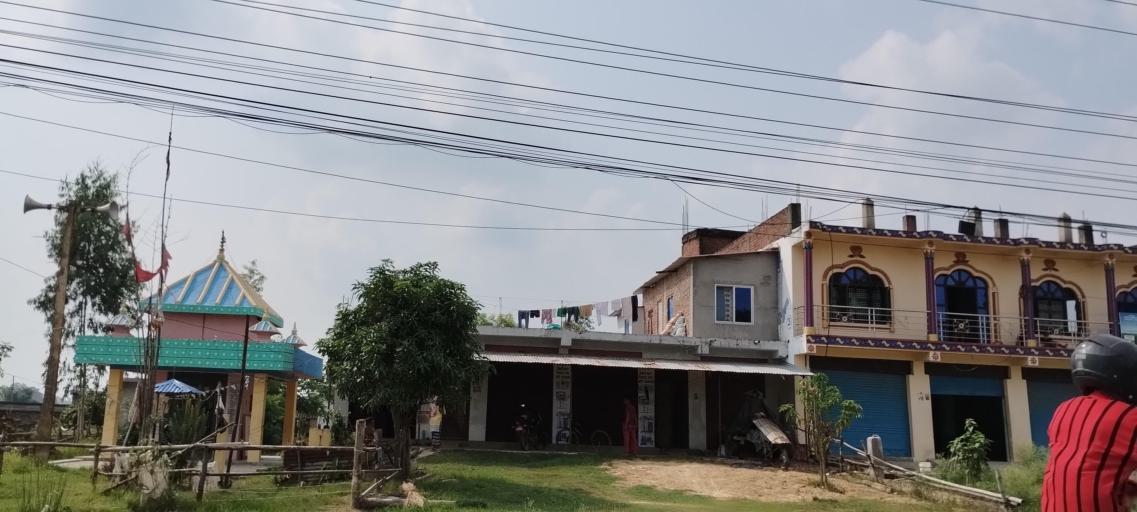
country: NP
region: Mid Western
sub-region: Bheri Zone
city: Nepalgunj
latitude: 28.1604
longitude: 81.6713
